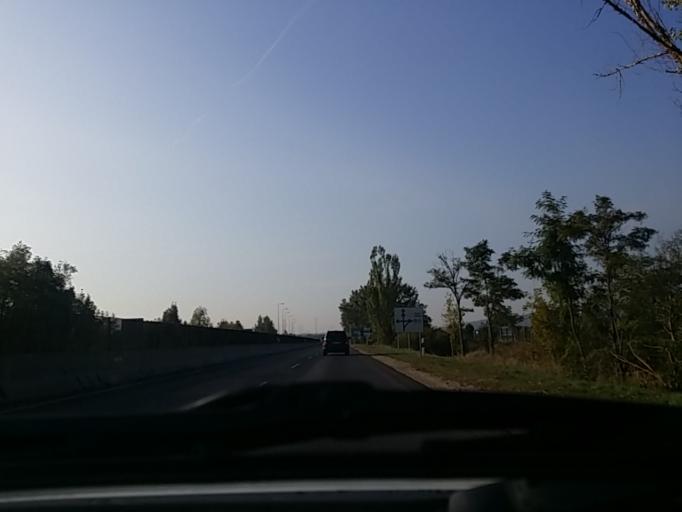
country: HU
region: Pest
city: Budakalasz
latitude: 47.6252
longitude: 19.0679
